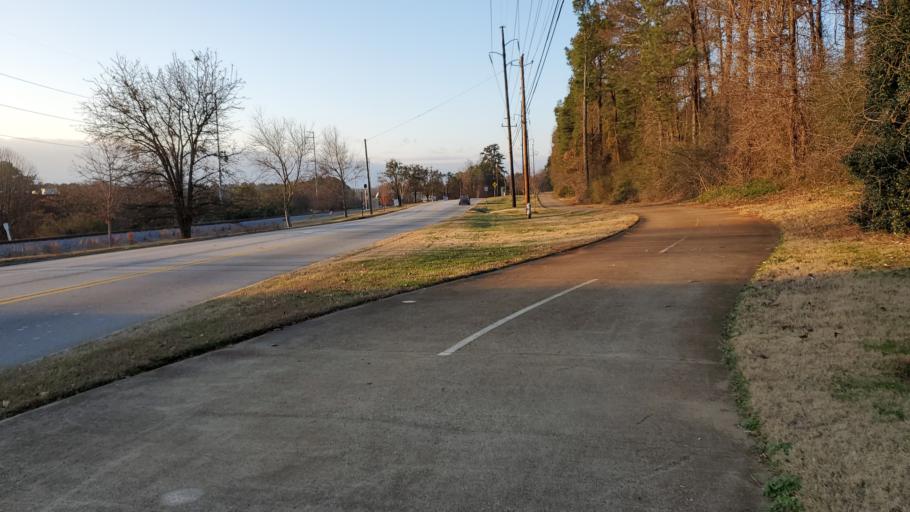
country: US
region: Georgia
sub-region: DeKalb County
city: Stone Mountain
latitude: 33.8189
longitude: -84.1852
